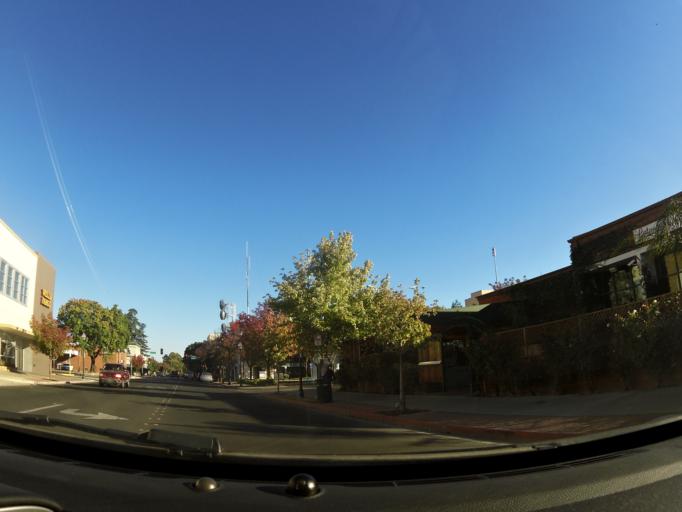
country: US
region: California
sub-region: Merced County
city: Merced
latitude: 37.3029
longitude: -120.4843
